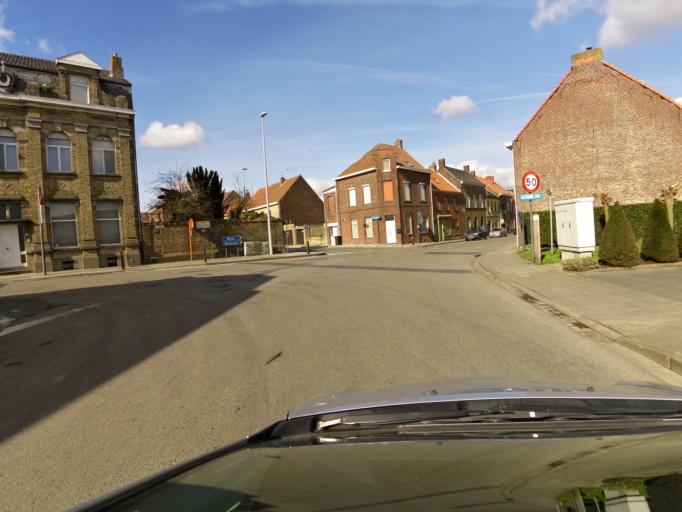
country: FR
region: Nord-Pas-de-Calais
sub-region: Departement du Nord
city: Nieppe
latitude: 50.7451
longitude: 2.8229
